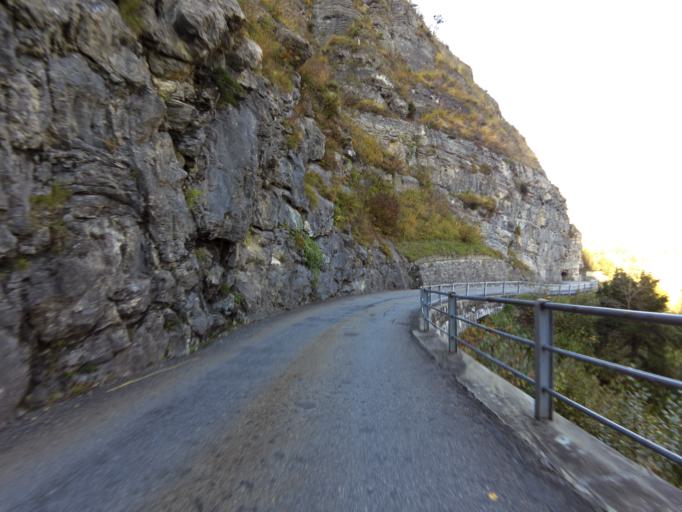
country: CH
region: Uri
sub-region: Uri
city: Bauen
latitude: 46.9158
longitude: 8.5934
